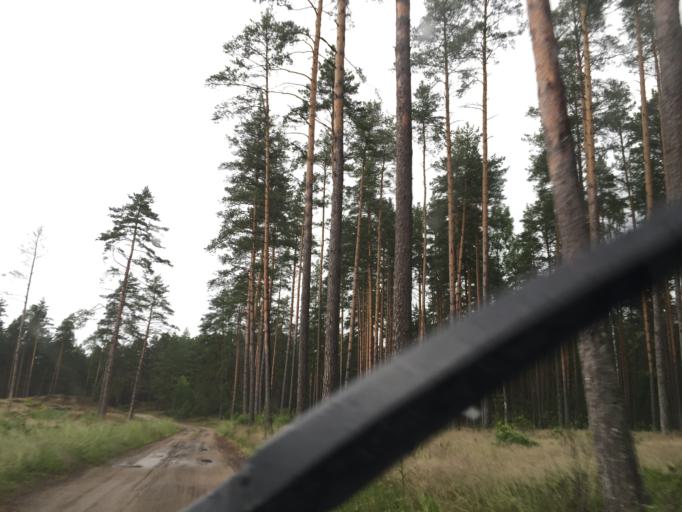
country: LV
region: Riga
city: Jaunciems
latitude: 57.0590
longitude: 24.2008
